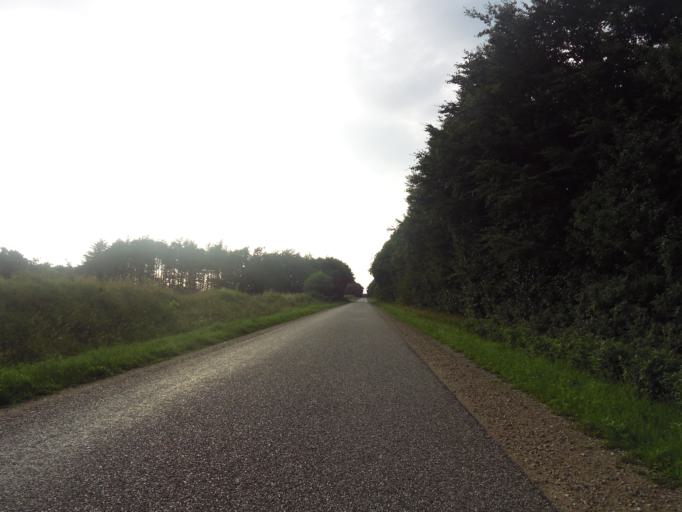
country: DK
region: South Denmark
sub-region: Tonder Kommune
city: Logumkloster
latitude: 55.1524
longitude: 8.9465
